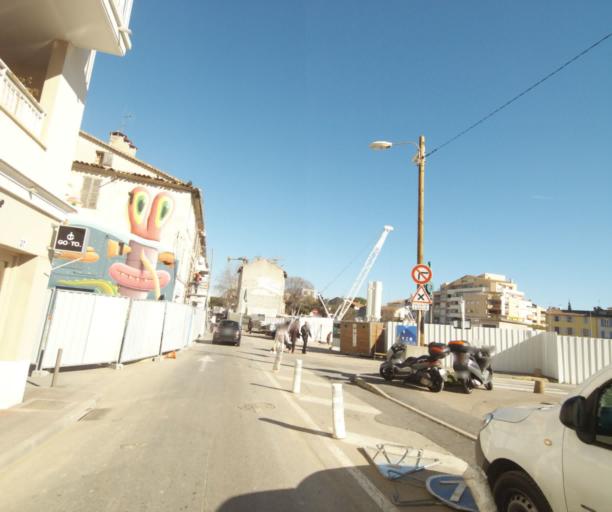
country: FR
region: Provence-Alpes-Cote d'Azur
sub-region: Departement des Alpes-Maritimes
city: Antibes
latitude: 43.5818
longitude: 7.1226
